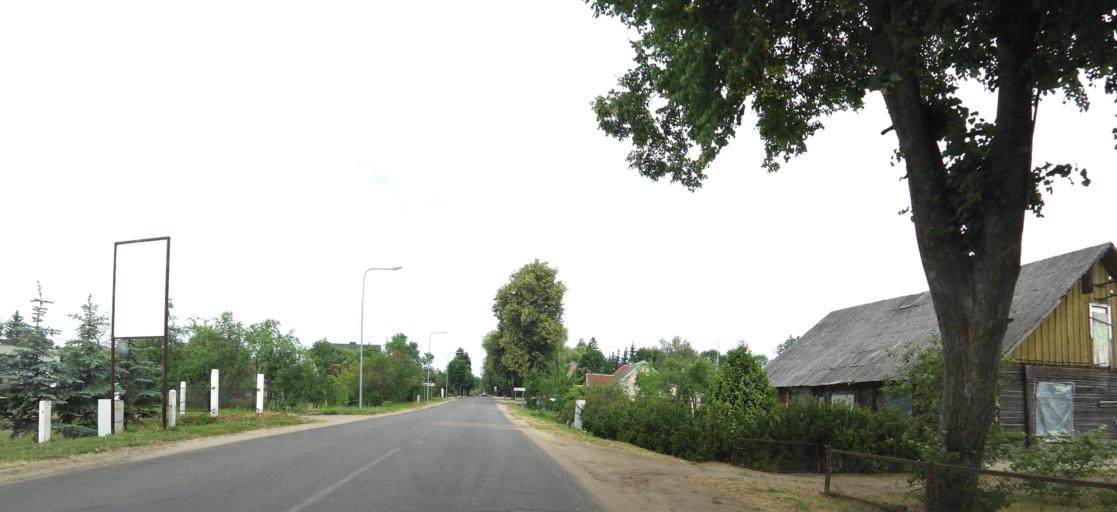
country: LT
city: Sirvintos
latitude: 55.0332
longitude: 24.9749
